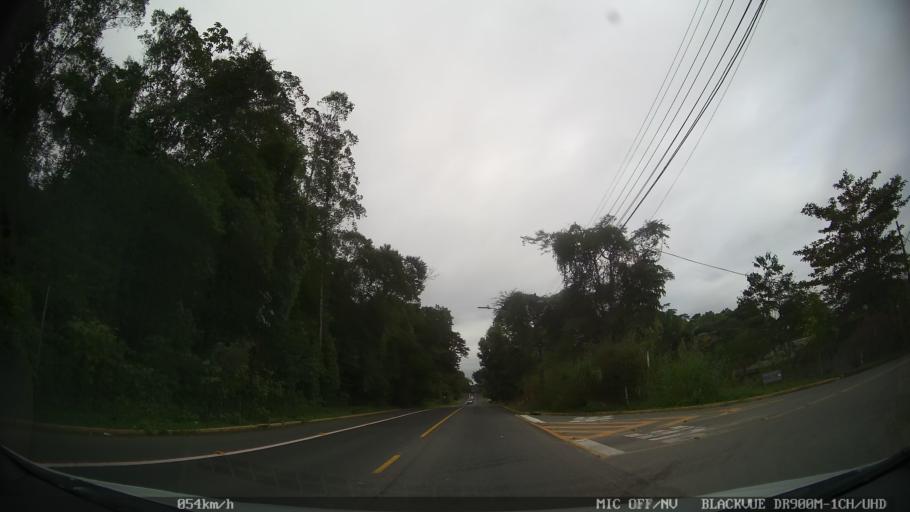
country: BR
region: Santa Catarina
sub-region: Joinville
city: Joinville
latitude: -26.3112
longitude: -48.8633
